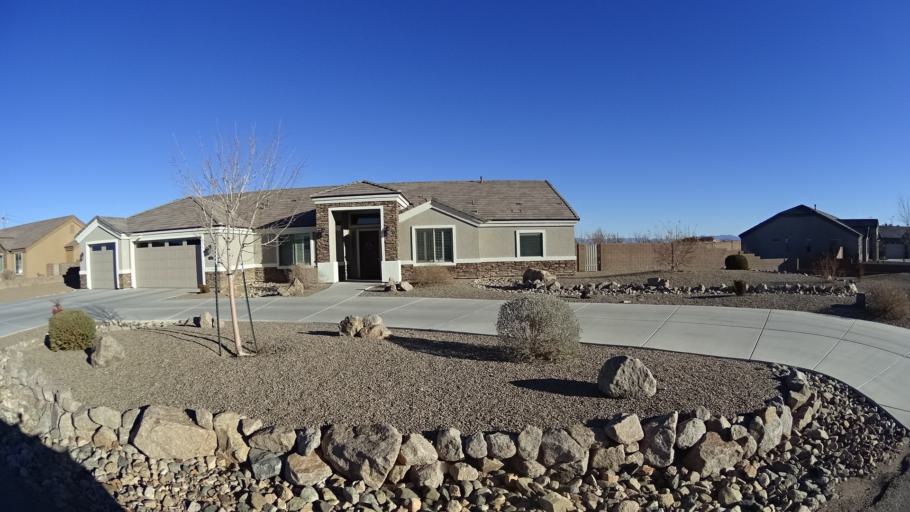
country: US
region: Arizona
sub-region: Mohave County
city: Kingman
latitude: 35.1949
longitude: -114.0017
